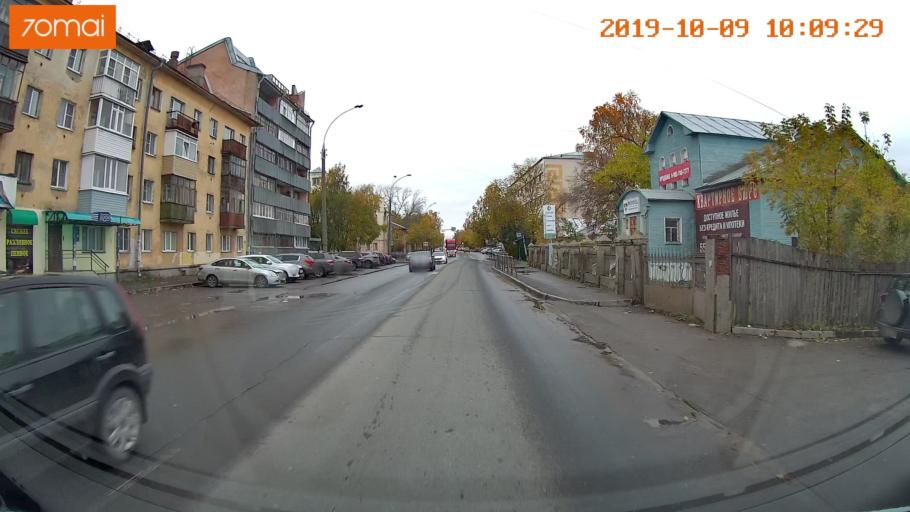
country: RU
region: Vologda
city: Vologda
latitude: 59.2120
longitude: 39.9038
